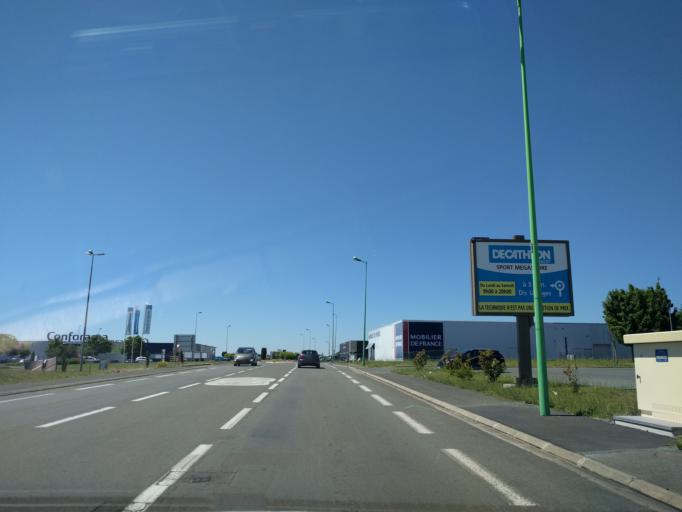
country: FR
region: Poitou-Charentes
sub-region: Departement des Deux-Sevres
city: Chauray
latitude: 46.3346
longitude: -0.4071
